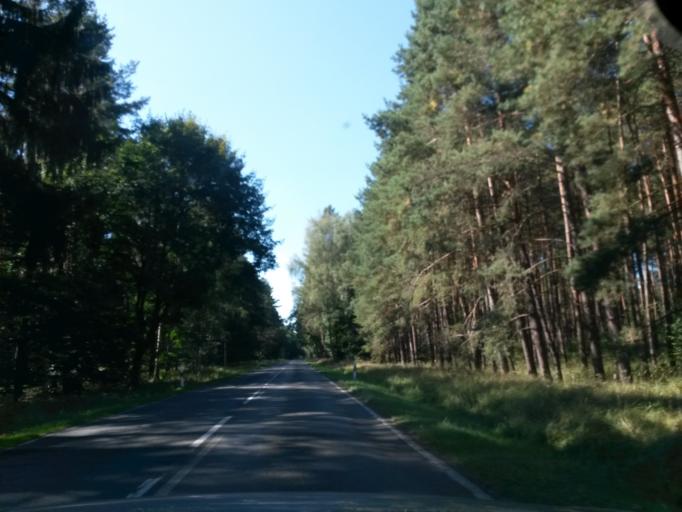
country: DE
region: Brandenburg
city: Lychen
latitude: 53.2428
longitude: 13.4084
